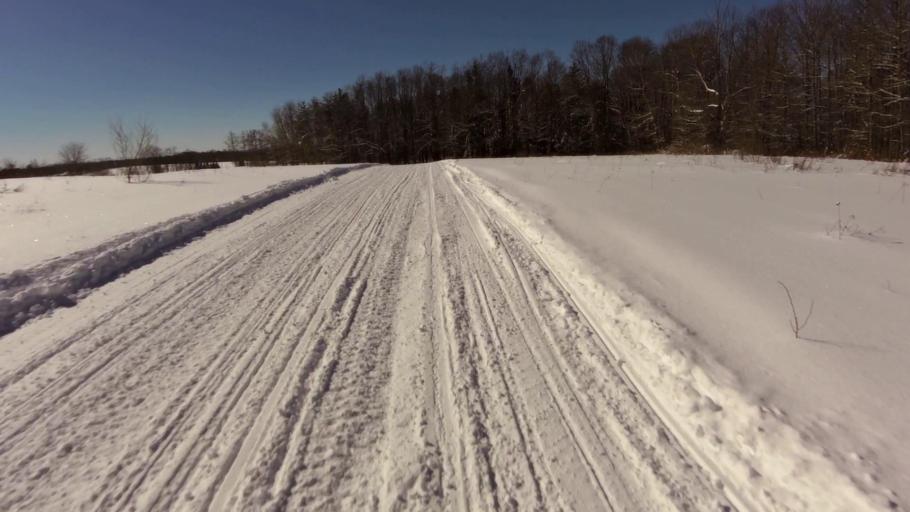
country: US
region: New York
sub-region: Chautauqua County
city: Mayville
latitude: 42.2293
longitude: -79.3926
